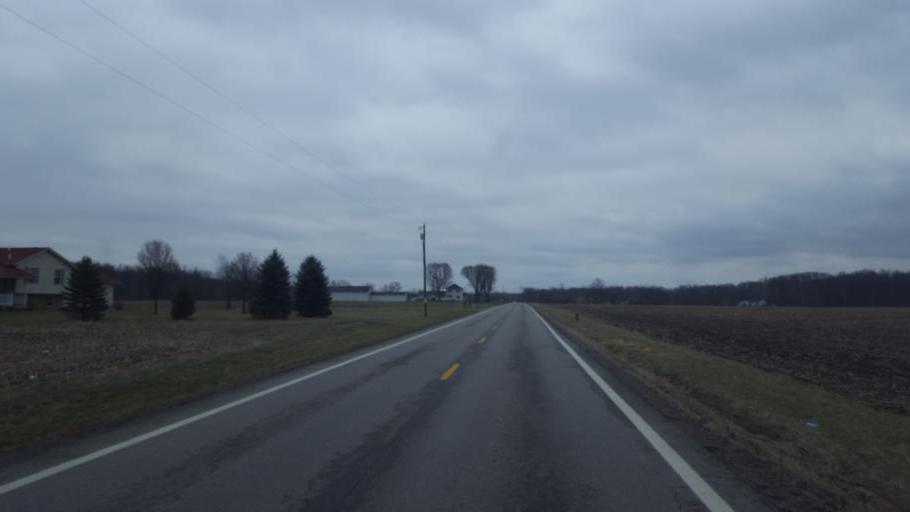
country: US
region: Ohio
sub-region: Delaware County
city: Ashley
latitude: 40.4227
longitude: -83.0322
